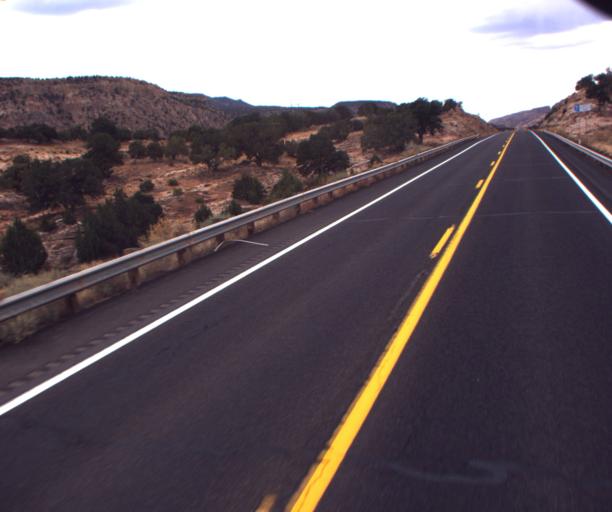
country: US
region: Arizona
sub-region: Navajo County
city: Kayenta
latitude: 36.6849
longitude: -110.3788
